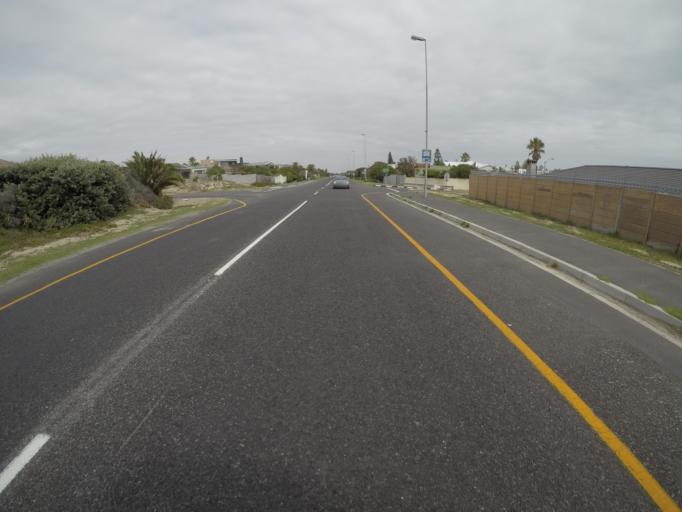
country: ZA
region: Western Cape
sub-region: City of Cape Town
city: Sunset Beach
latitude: -33.7173
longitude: 18.4458
